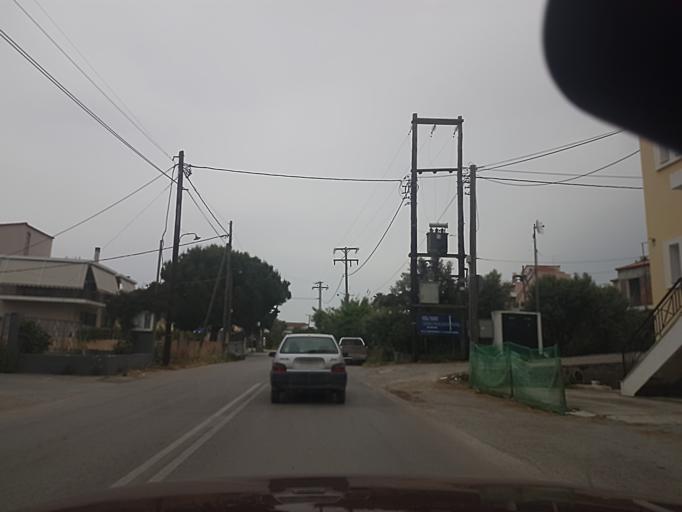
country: GR
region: Central Greece
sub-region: Nomos Evvoias
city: Chalkida
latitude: 38.4658
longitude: 23.6277
